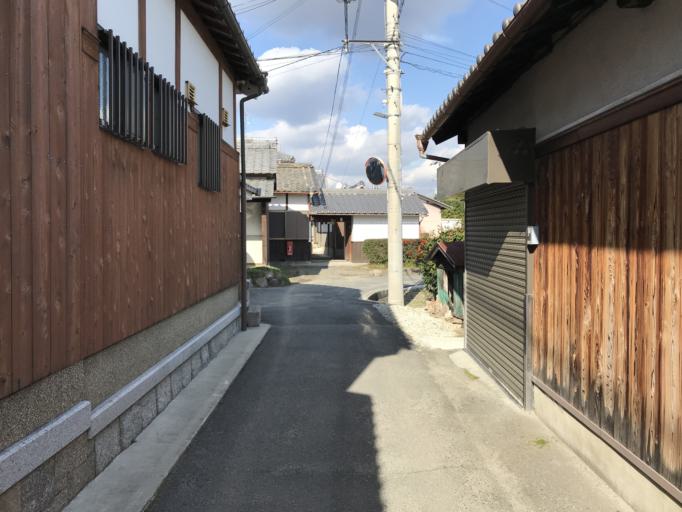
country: JP
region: Nara
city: Nara-shi
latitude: 34.6682
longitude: 135.7869
